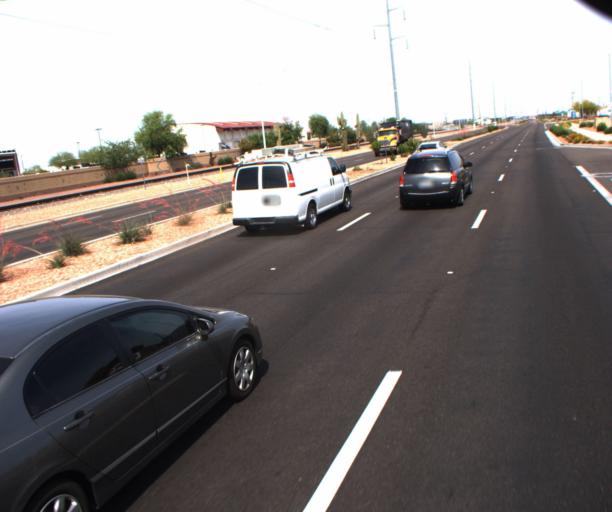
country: US
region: Arizona
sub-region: Maricopa County
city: Glendale
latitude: 33.5439
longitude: -112.1922
